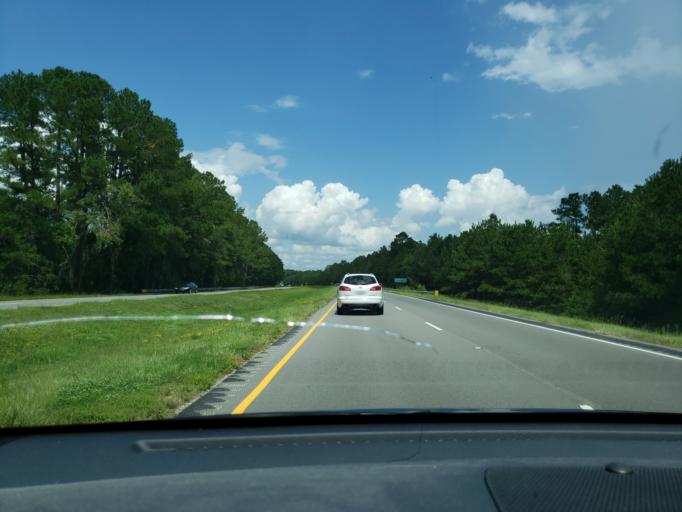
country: US
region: North Carolina
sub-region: Robeson County
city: Saint Pauls
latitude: 34.8508
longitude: -78.8517
